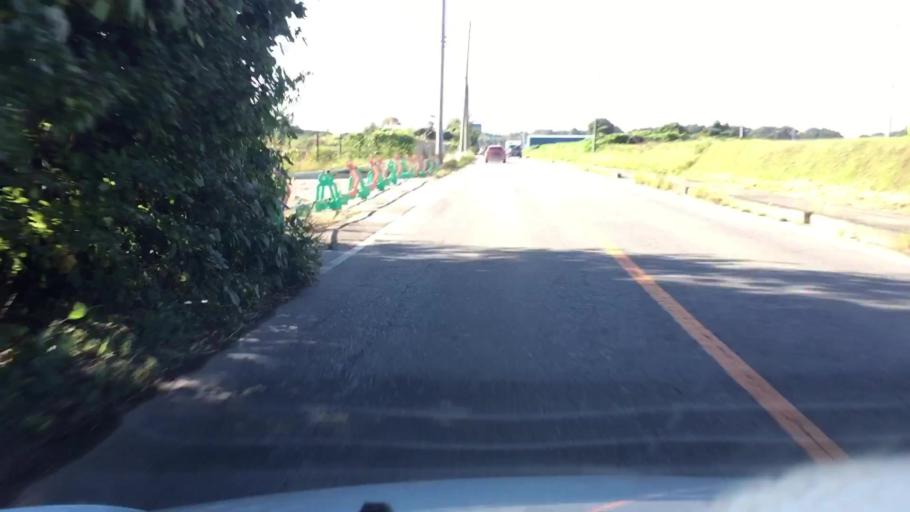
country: JP
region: Tochigi
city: Ujiie
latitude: 36.5849
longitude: 139.9829
